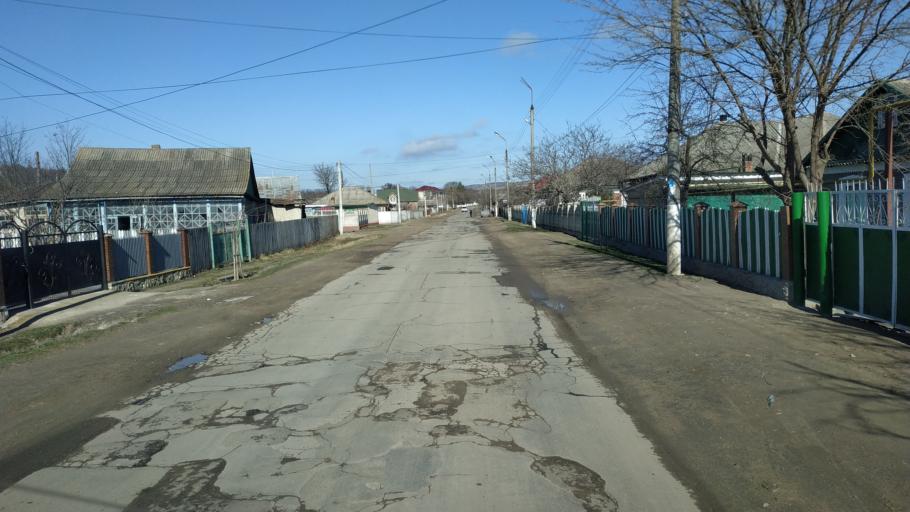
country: MD
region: Hincesti
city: Hincesti
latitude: 46.9572
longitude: 28.6055
